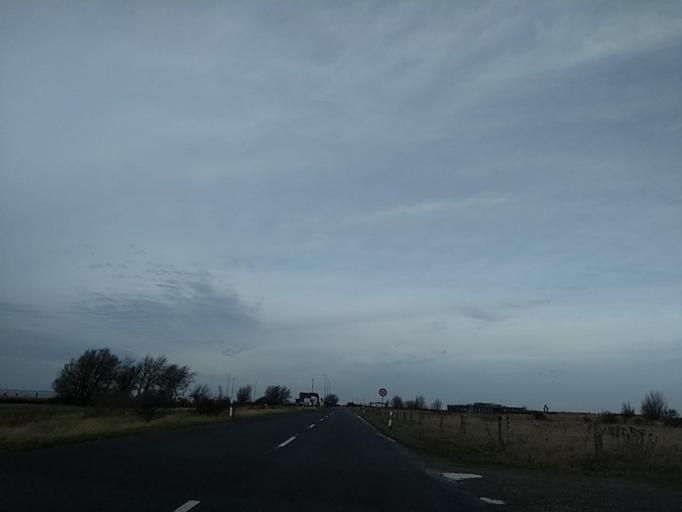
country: NL
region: Groningen
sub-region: Gemeente Delfzijl
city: Delfzijl
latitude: 53.3532
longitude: 7.0064
